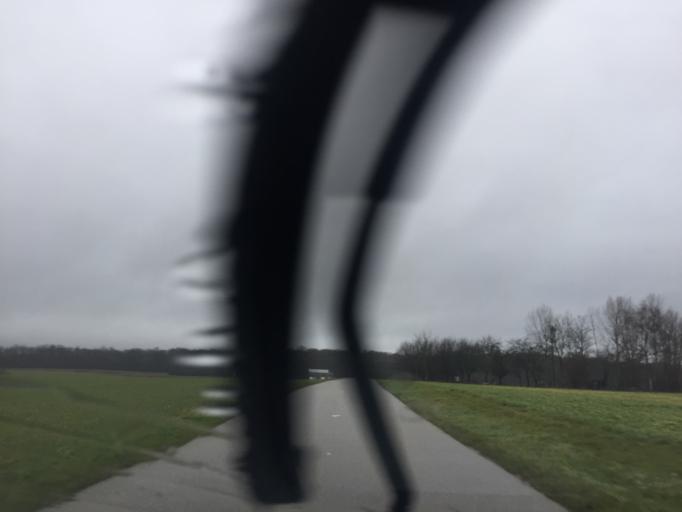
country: FR
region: Franche-Comte
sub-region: Departement du Jura
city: Dole
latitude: 47.1086
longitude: 5.5340
